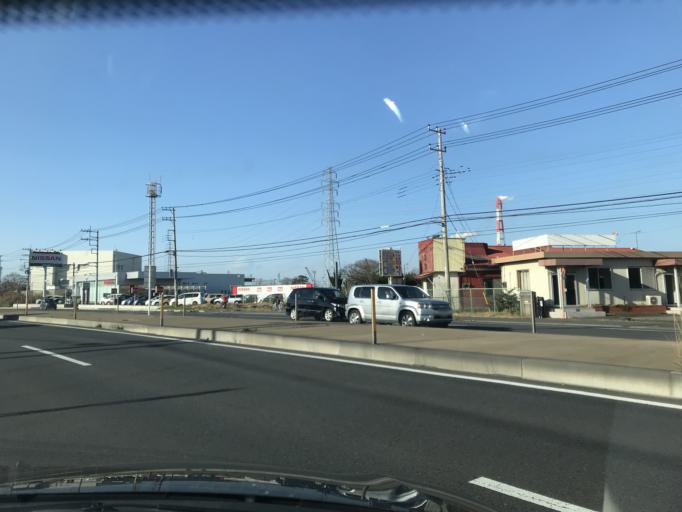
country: JP
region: Chiba
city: Omigawa
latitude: 35.8789
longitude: 140.6854
